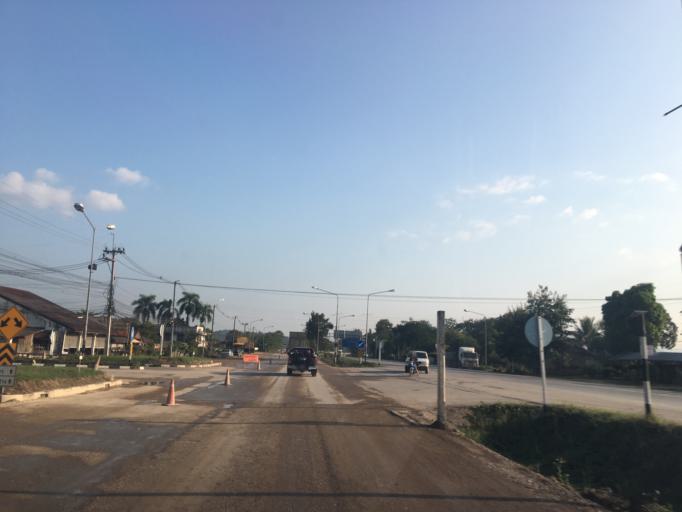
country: TH
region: Lampang
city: Ngao
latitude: 18.7465
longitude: 99.9733
